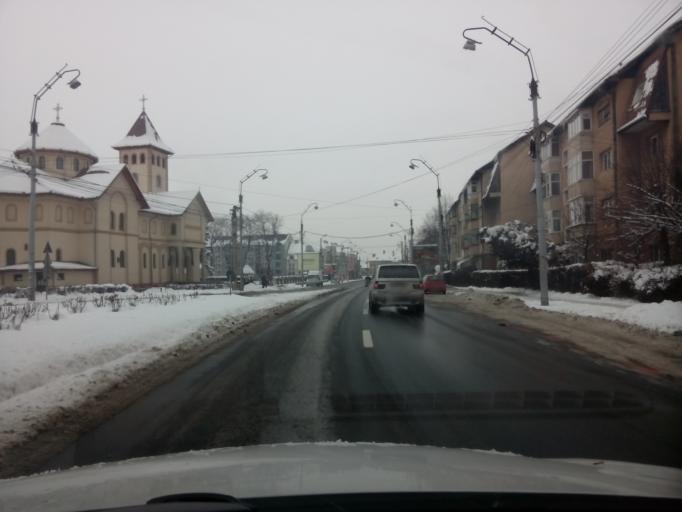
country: RO
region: Sibiu
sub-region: Municipiul Sibiu
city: Sibiu
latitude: 45.7968
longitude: 24.1588
